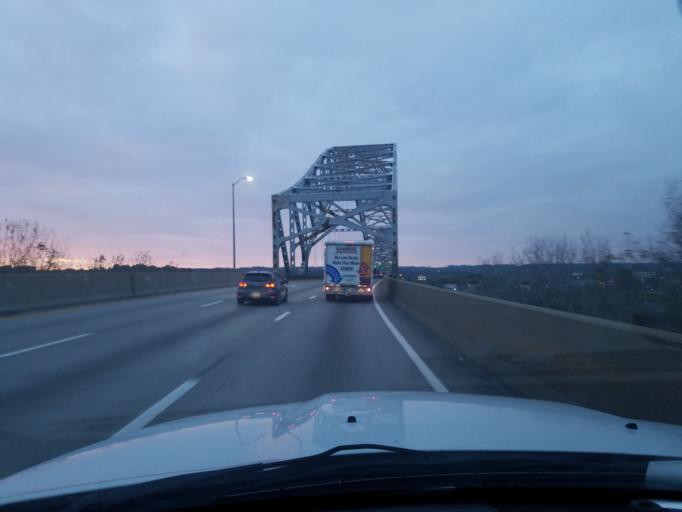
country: US
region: Indiana
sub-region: Floyd County
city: New Albany
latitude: 38.2760
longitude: -85.8199
